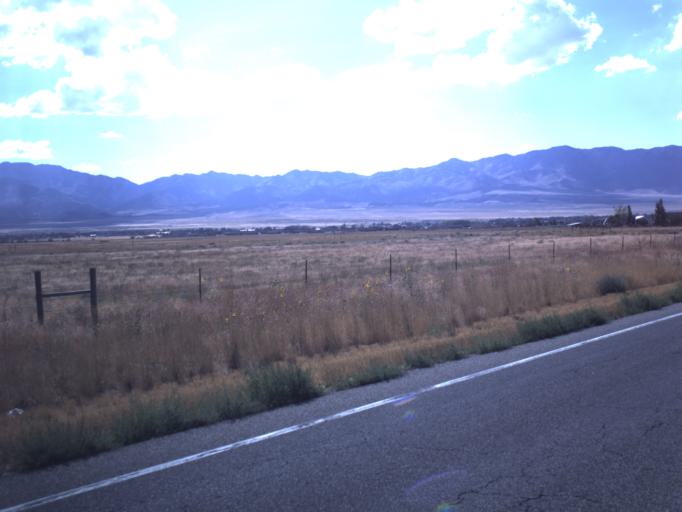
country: US
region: Utah
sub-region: Tooele County
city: Grantsville
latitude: 40.5839
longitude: -112.4059
